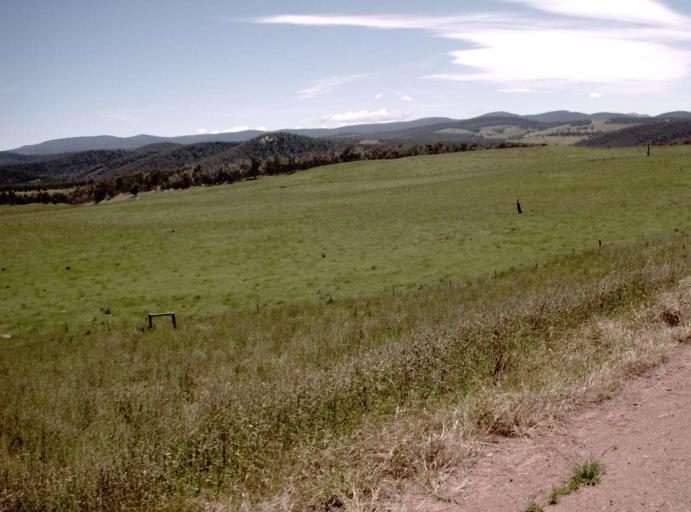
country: AU
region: New South Wales
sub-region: Snowy River
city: Jindabyne
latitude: -37.0908
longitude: 148.2548
